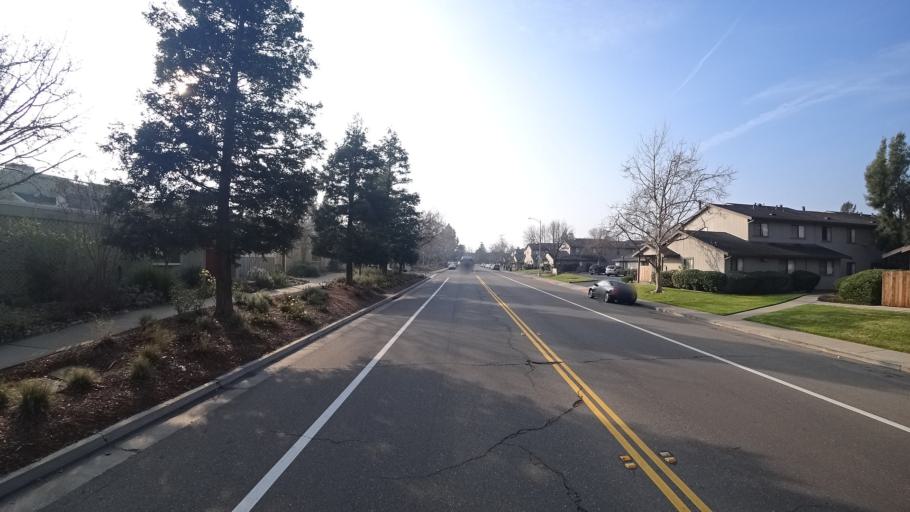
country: US
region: California
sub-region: Yolo County
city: Davis
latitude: 38.5652
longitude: -121.7657
